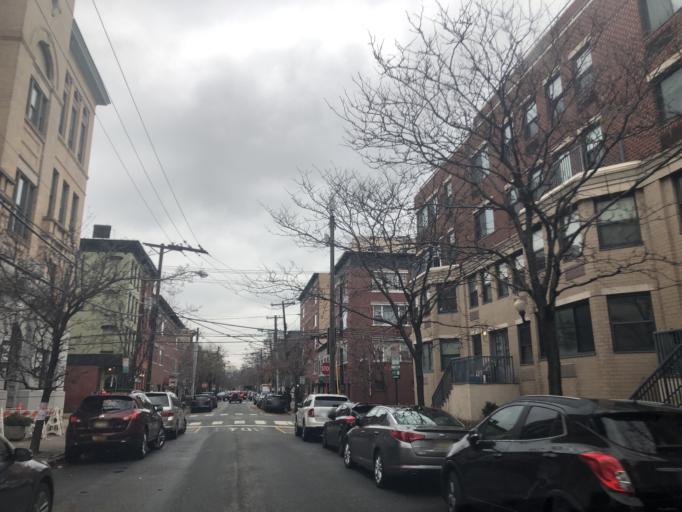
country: US
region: New Jersey
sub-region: Hudson County
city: Hoboken
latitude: 40.7370
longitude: -74.0339
